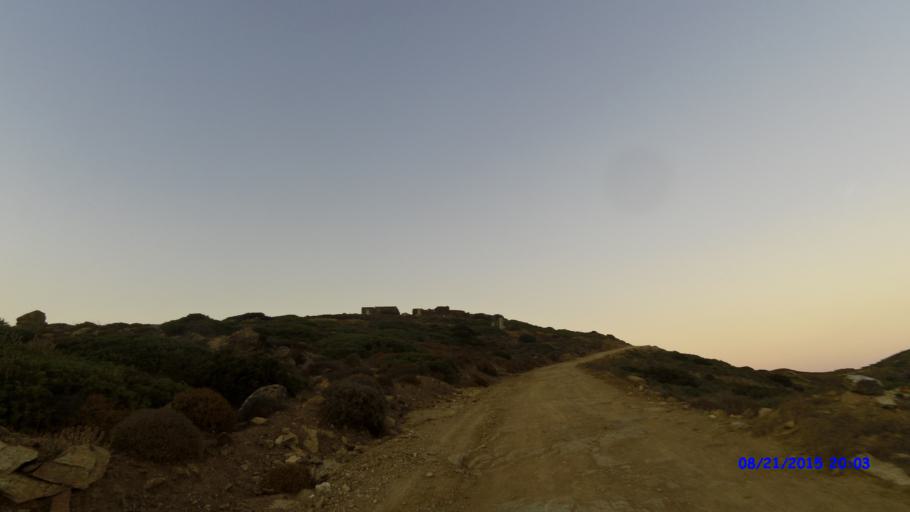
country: GR
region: South Aegean
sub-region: Nomos Kykladon
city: Antiparos
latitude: 37.0071
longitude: 25.0390
